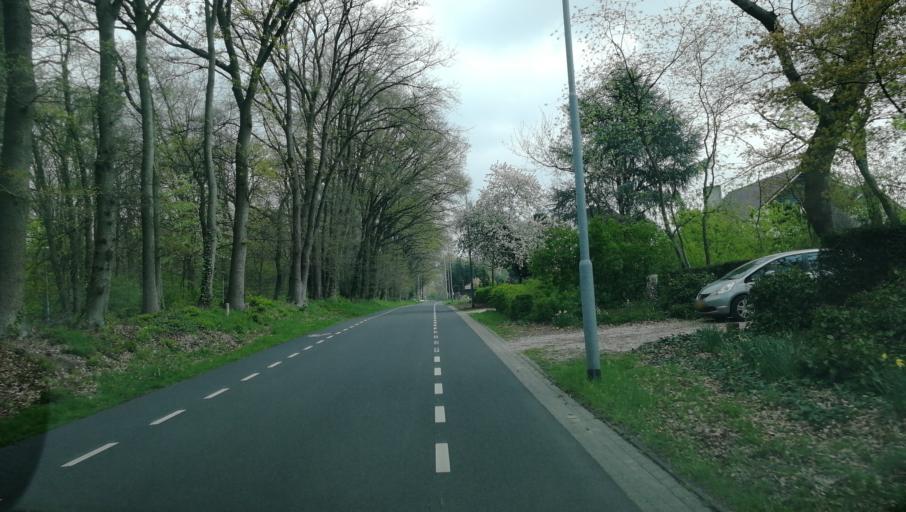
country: NL
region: Limburg
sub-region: Gemeente Venlo
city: Venlo
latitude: 51.3577
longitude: 6.1942
